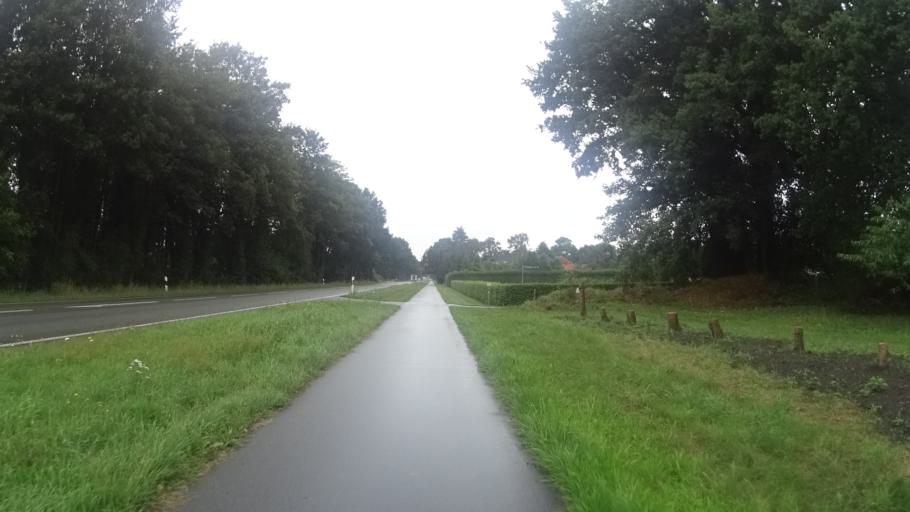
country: DE
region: Lower Saxony
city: Holtland
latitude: 53.2820
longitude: 7.5775
